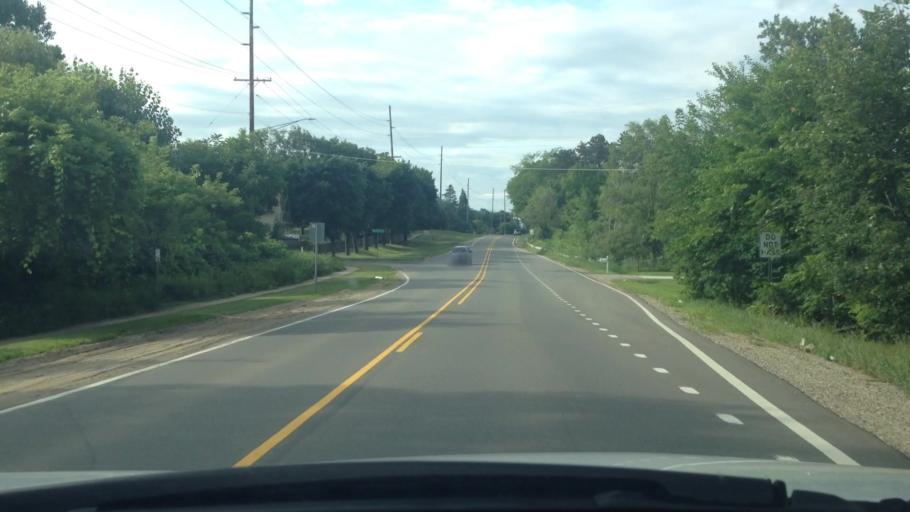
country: US
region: Michigan
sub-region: Oakland County
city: Waterford
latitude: 42.6993
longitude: -83.3486
